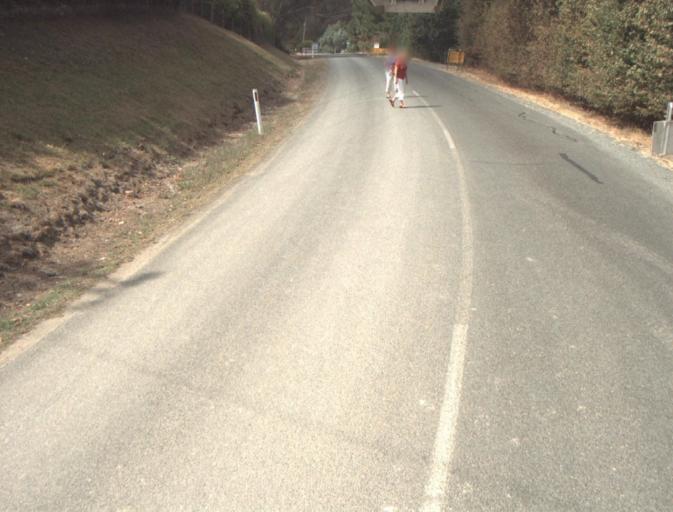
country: AU
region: Tasmania
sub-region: Launceston
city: Mayfield
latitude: -41.3155
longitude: 147.0383
